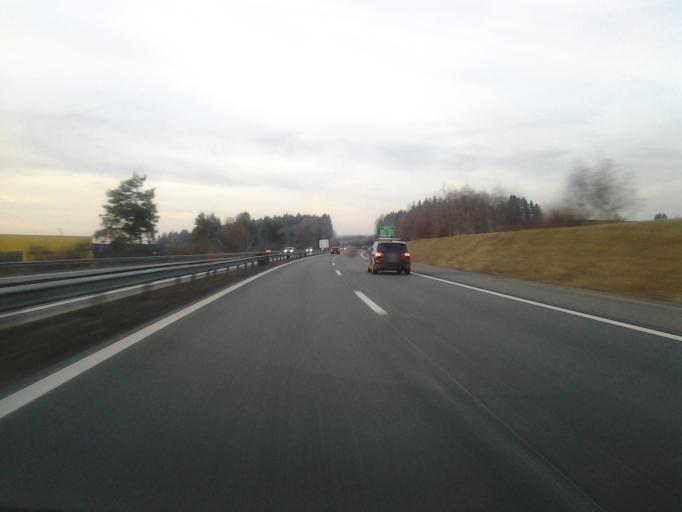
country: CH
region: Lucerne
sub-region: Hochdorf District
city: Emmen
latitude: 47.0953
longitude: 8.2461
